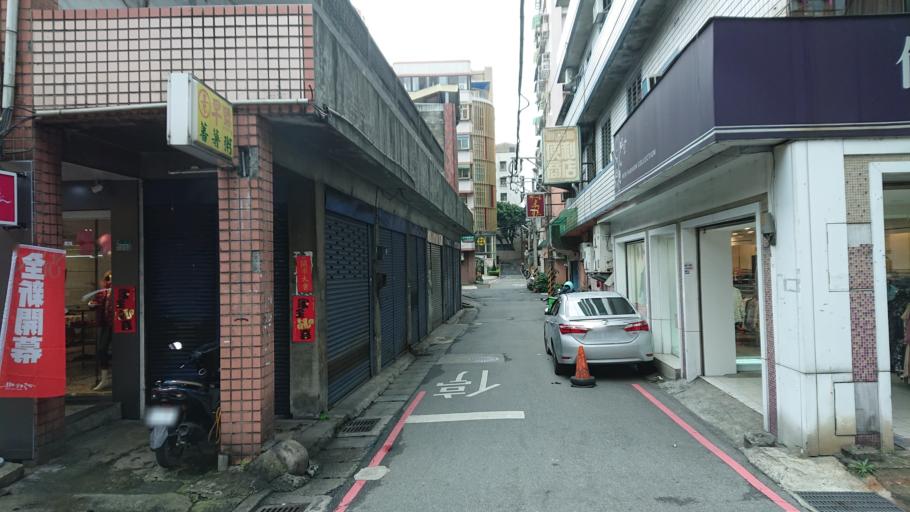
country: TW
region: Taiwan
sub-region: Taoyuan
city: Taoyuan
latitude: 24.9541
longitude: 121.3505
